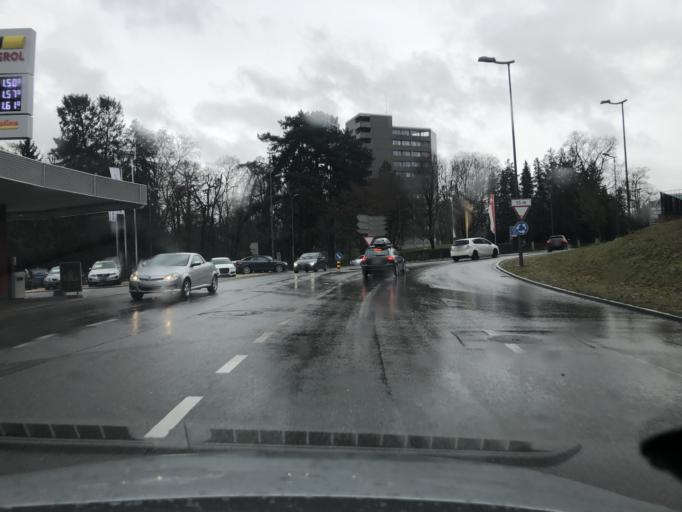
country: CH
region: Aargau
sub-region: Bezirk Brugg
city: Brugg
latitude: 47.4820
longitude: 8.2122
